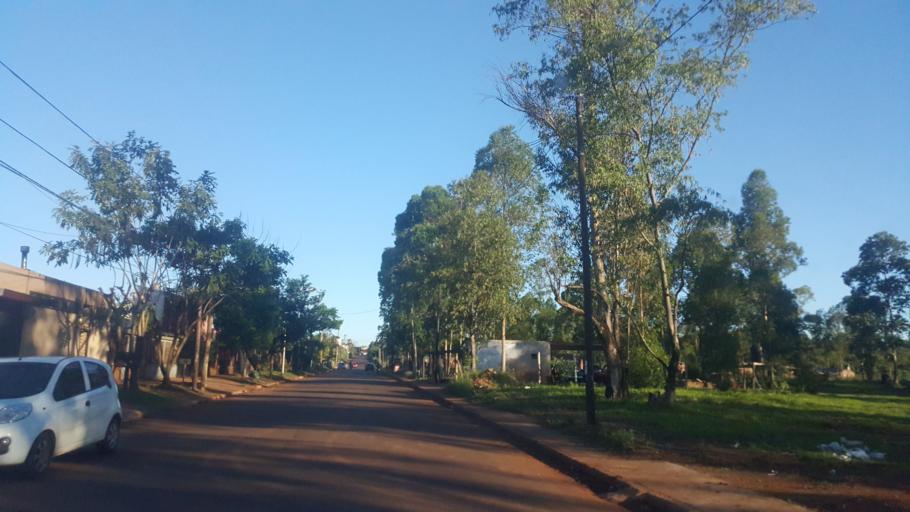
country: AR
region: Misiones
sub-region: Departamento de Capital
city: Posadas
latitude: -27.4253
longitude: -55.9410
